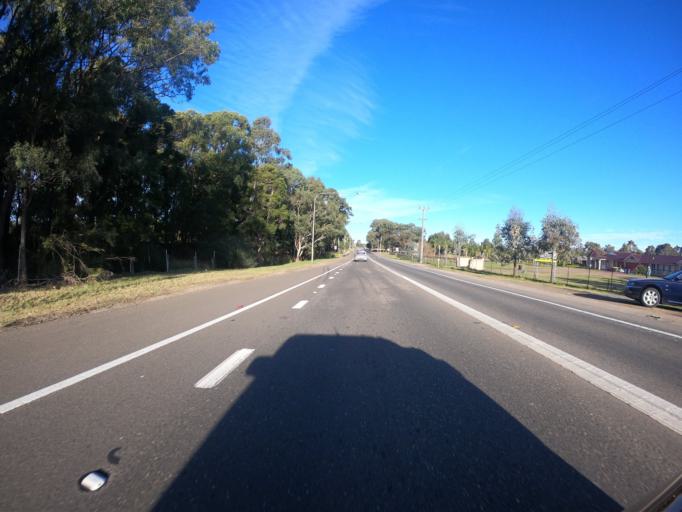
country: AU
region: New South Wales
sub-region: Hawkesbury
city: South Windsor
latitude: -33.6690
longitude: 150.8042
